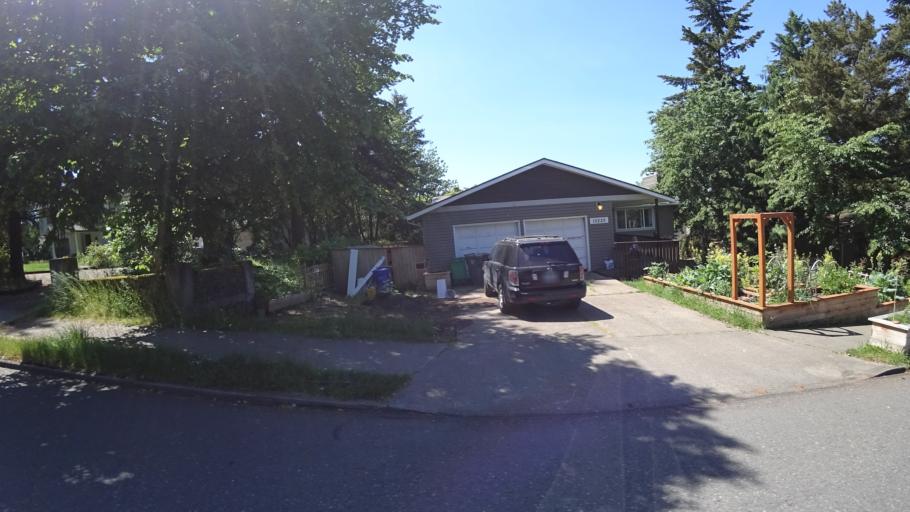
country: US
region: Oregon
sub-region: Washington County
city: Metzger
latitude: 45.4515
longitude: -122.7129
